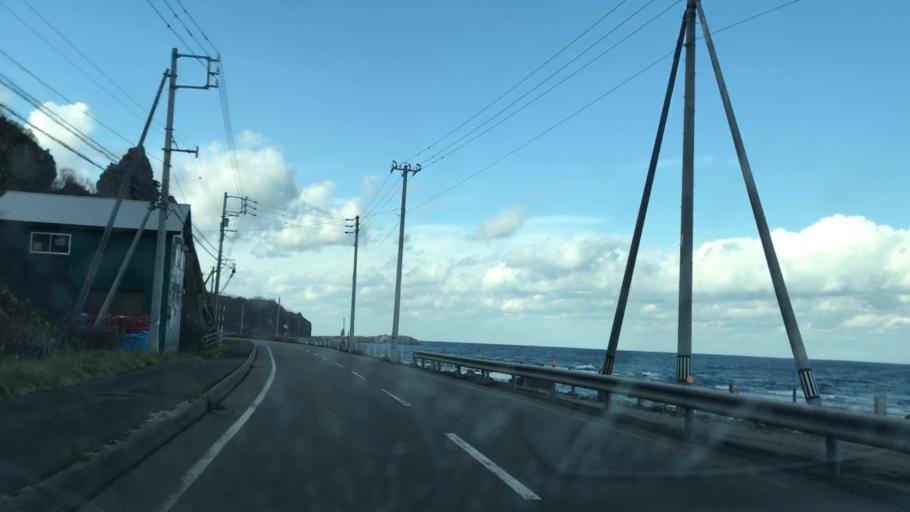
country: JP
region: Hokkaido
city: Iwanai
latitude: 43.3317
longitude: 140.3912
